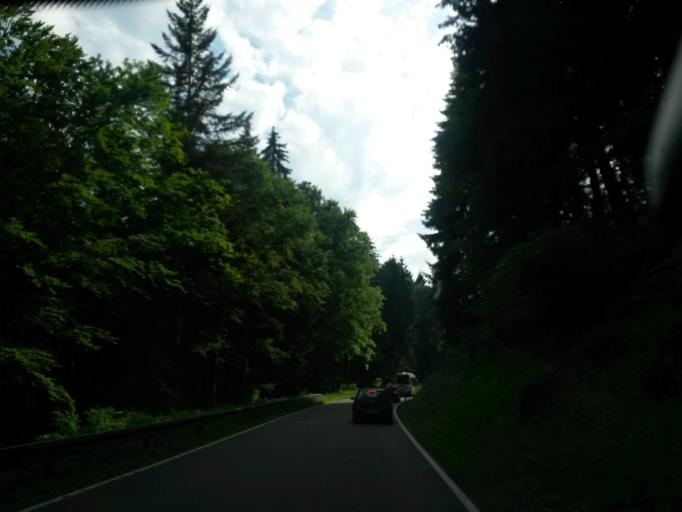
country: DE
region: Baden-Wuerttemberg
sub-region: Karlsruhe Region
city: Oberreichenbach
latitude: 48.7384
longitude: 8.6907
